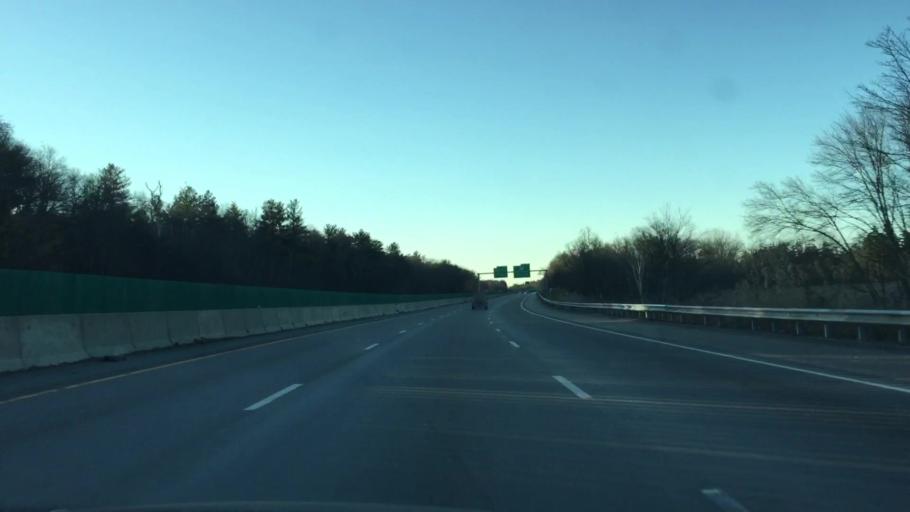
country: US
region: Massachusetts
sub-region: Plymouth County
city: West Bridgewater
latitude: 41.9804
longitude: -71.0255
